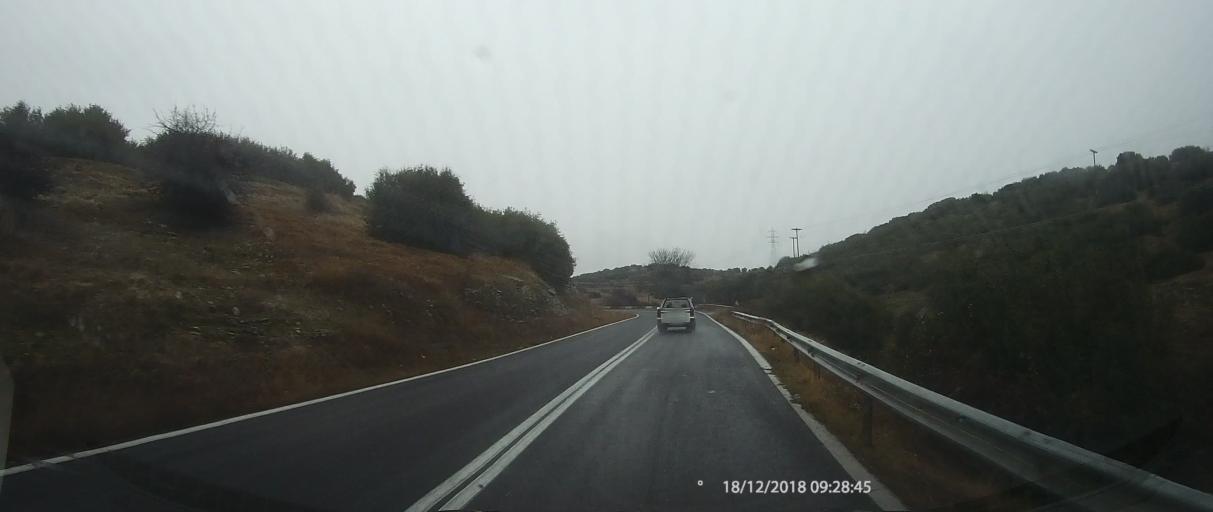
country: GR
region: Thessaly
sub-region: Nomos Larisis
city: Elassona
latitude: 39.9218
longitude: 22.1717
